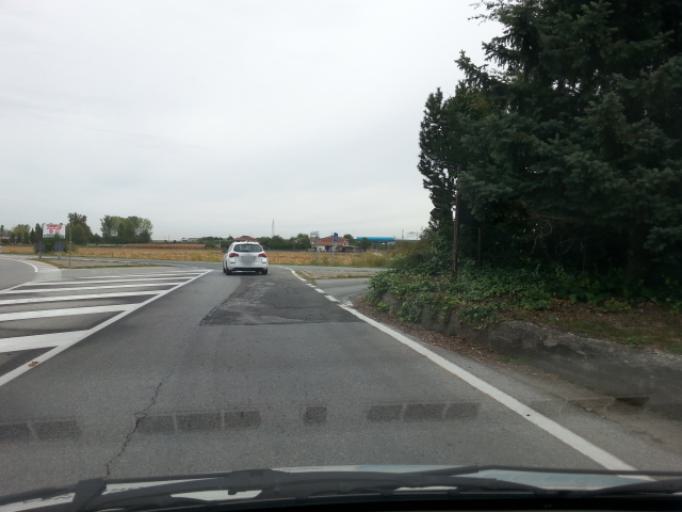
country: IT
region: Piedmont
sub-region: Provincia di Torino
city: Pinerolo
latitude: 44.8940
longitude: 7.3550
